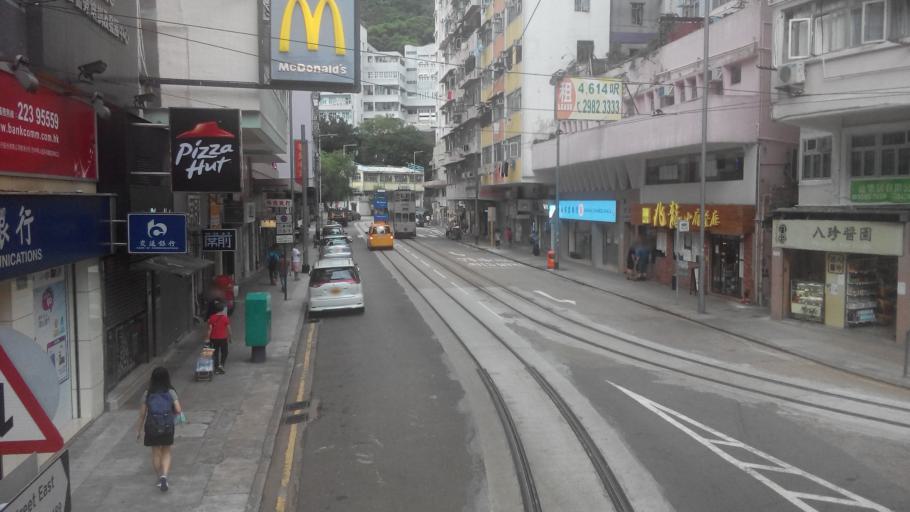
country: HK
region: Wanchai
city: Wan Chai
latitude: 22.2777
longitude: 114.2303
